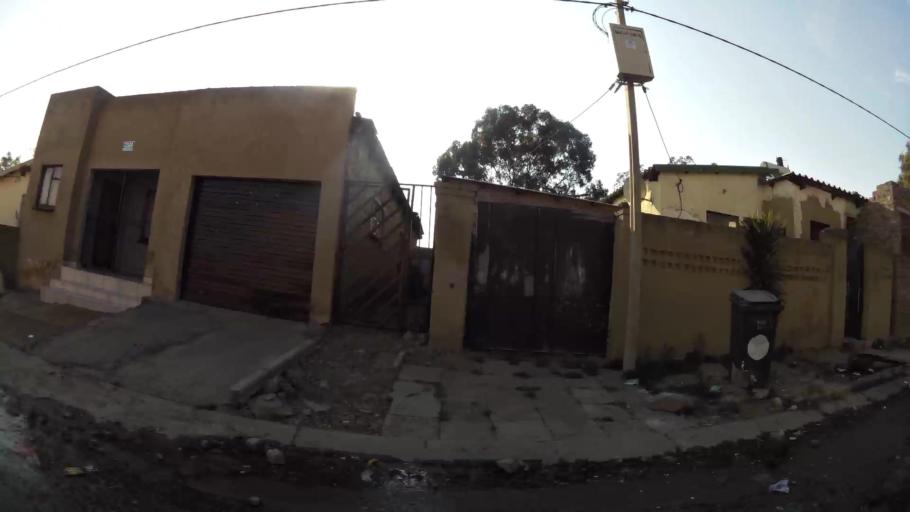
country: ZA
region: Gauteng
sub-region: City of Johannesburg Metropolitan Municipality
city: Modderfontein
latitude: -26.0962
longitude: 28.1101
